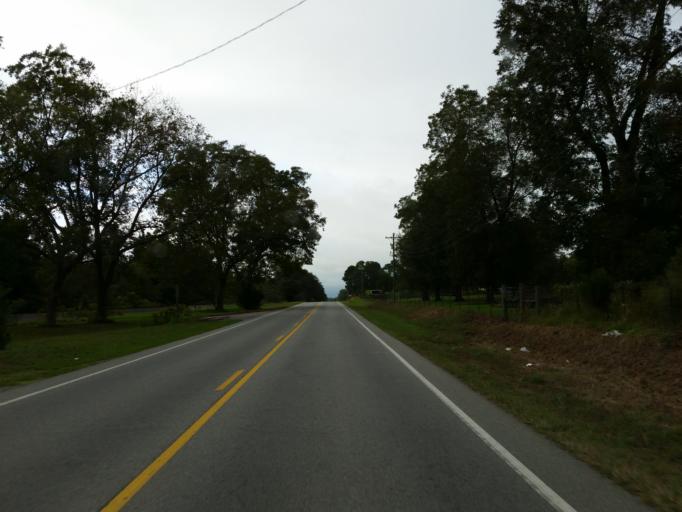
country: US
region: Georgia
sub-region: Tift County
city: Tifton
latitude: 31.5717
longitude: -83.5666
